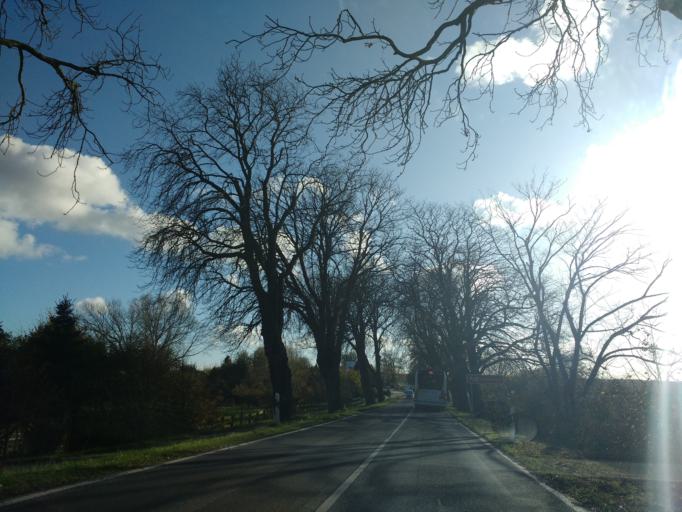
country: DE
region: Mecklenburg-Vorpommern
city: Grevesmuhlen
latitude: 53.9061
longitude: 11.1630
